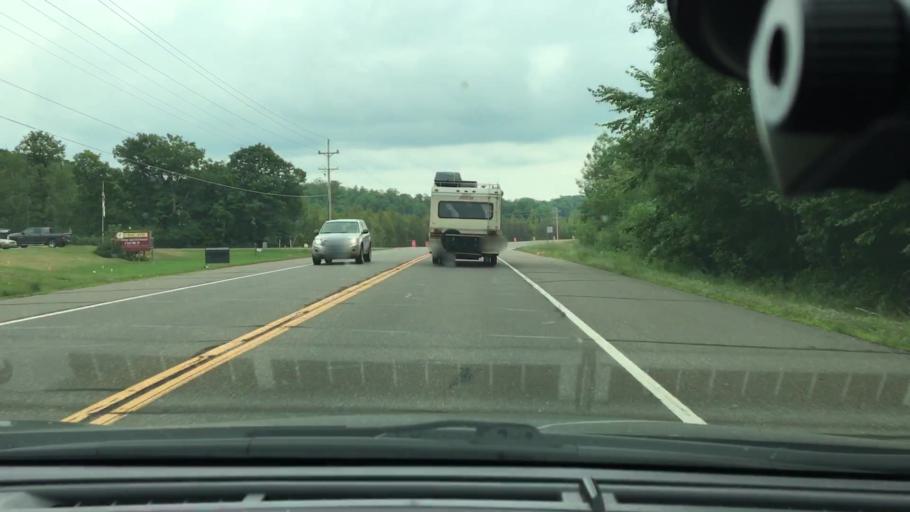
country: US
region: Minnesota
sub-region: Crow Wing County
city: Crosby
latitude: 46.4869
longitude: -93.9015
